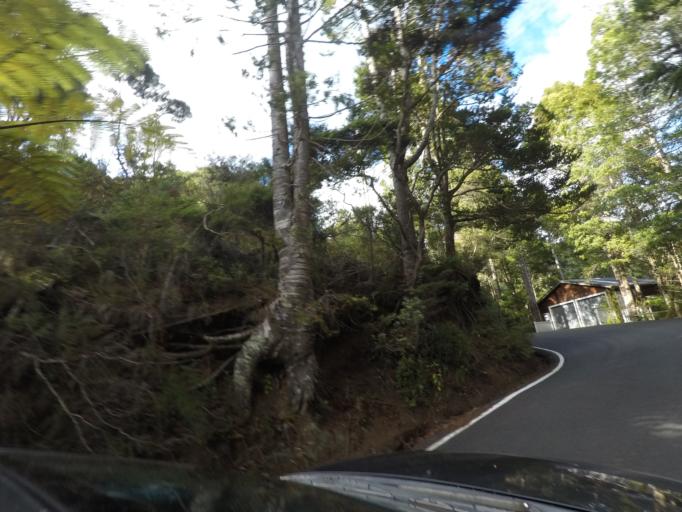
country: NZ
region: Auckland
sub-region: Auckland
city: Titirangi
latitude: -37.0175
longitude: 174.5514
